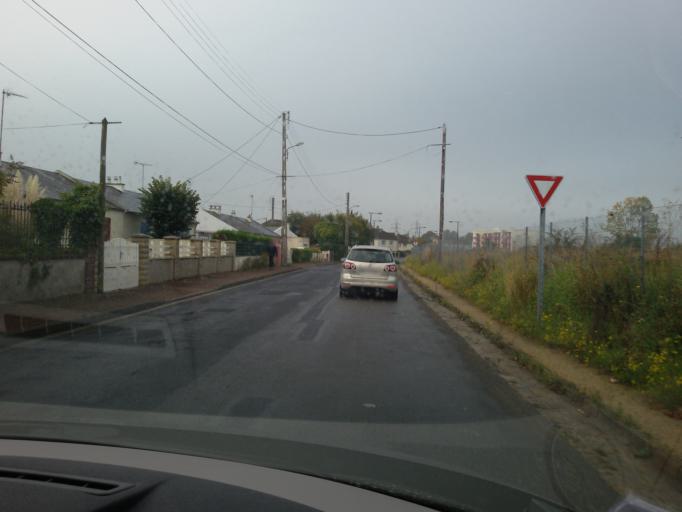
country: FR
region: Lower Normandy
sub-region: Departement du Calvados
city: Dives-sur-Mer
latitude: 49.2885
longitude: -0.1042
